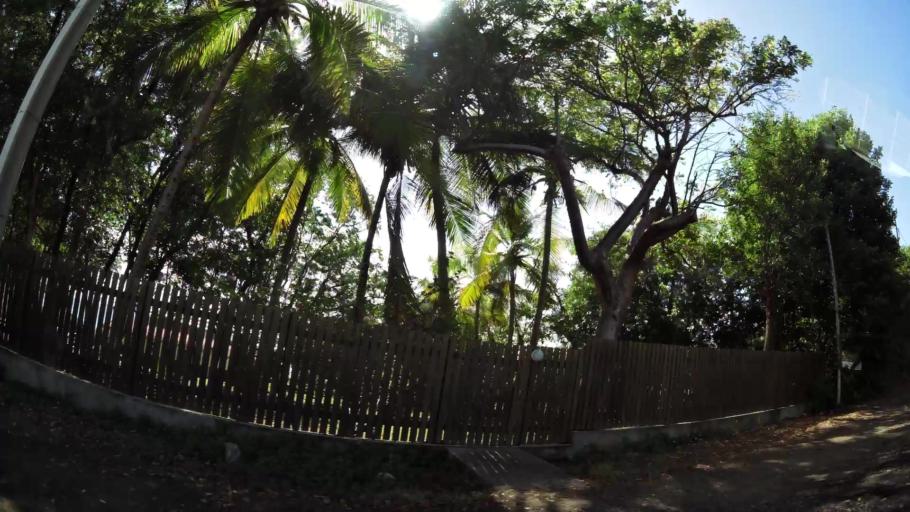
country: MQ
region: Martinique
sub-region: Martinique
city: Les Trois-Ilets
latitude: 14.4709
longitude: -61.0454
